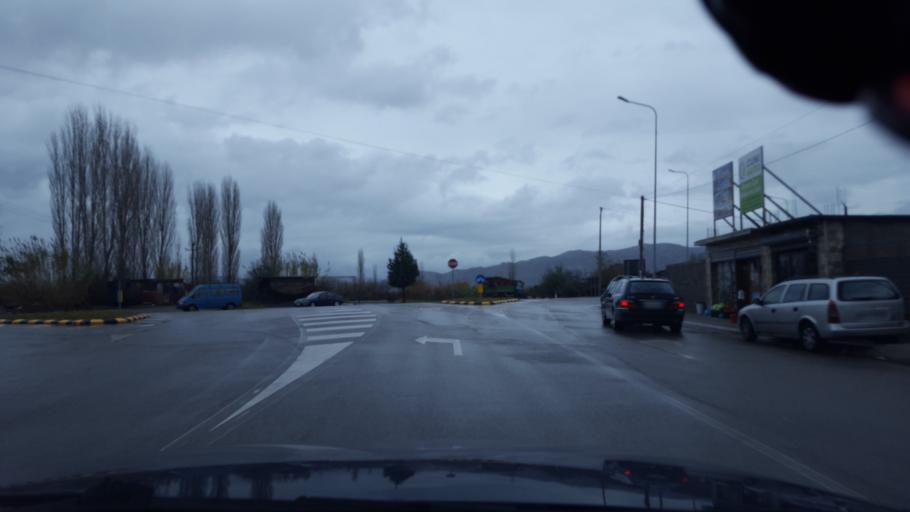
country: AL
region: Shkoder
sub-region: Rrethi i Malesia e Madhe
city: Kuc
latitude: 42.0318
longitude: 19.5026
